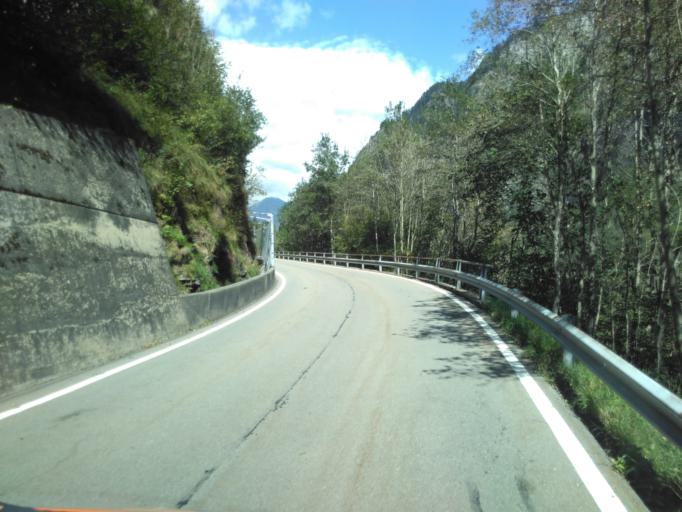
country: CH
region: Grisons
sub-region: Moesa District
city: Cauco
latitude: 46.3245
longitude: 9.1179
